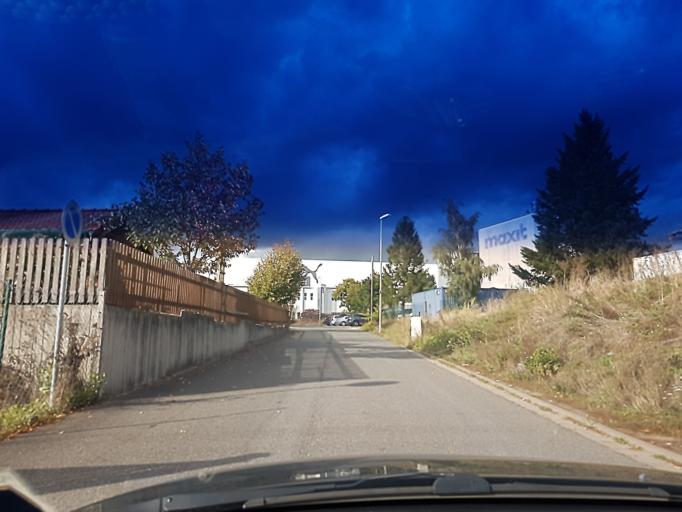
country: DE
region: Bavaria
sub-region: Regierungsbezirk Mittelfranken
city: Wachenroth
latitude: 49.7449
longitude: 10.6737
